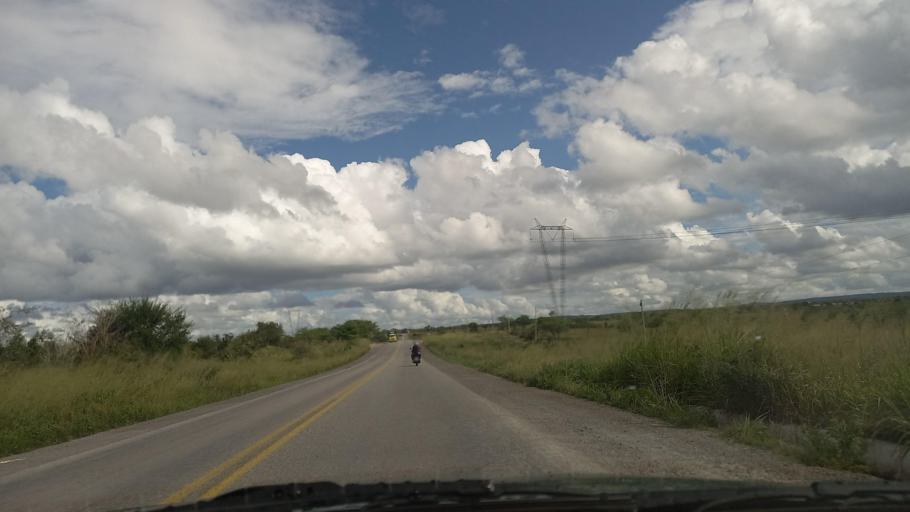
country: BR
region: Pernambuco
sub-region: Lajedo
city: Lajedo
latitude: -8.5986
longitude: -36.2919
